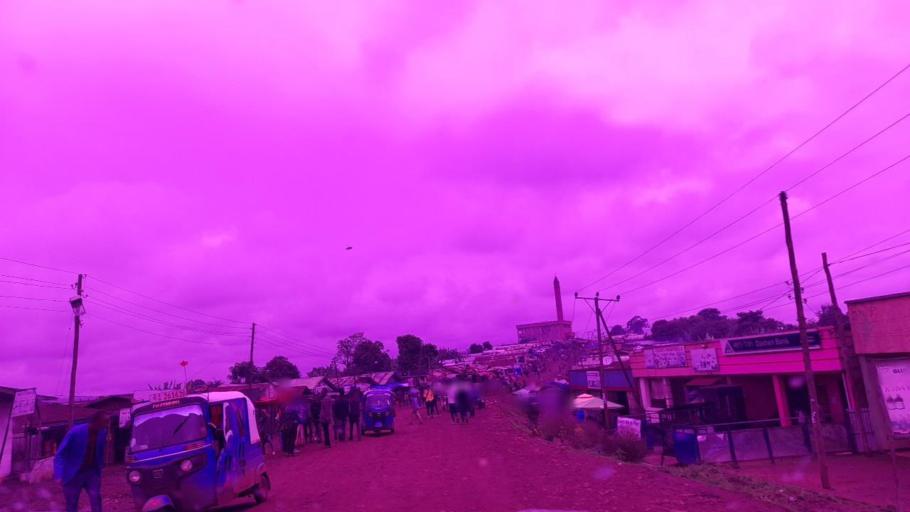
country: ET
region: Southern Nations, Nationalities, and People's Region
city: Tippi
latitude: 7.5936
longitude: 35.7582
